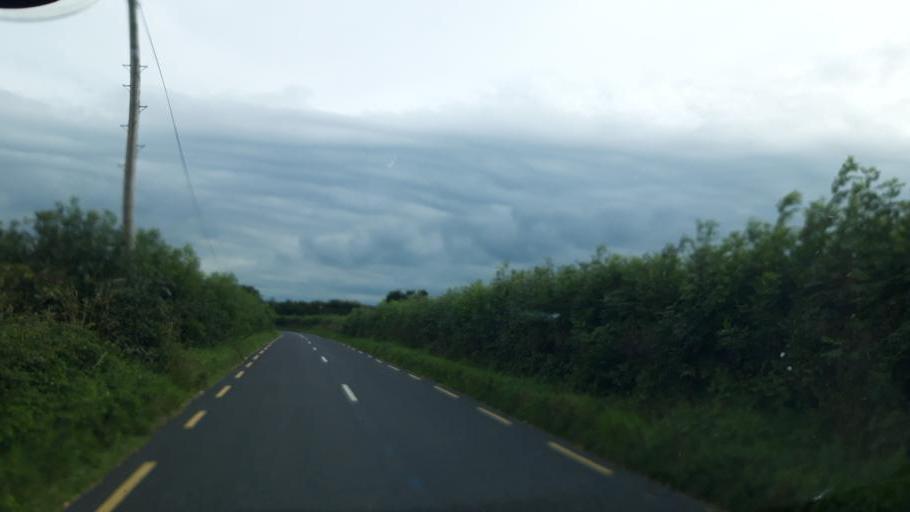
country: IE
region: Leinster
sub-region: Kilkenny
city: Ballyragget
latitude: 52.7531
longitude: -7.3921
